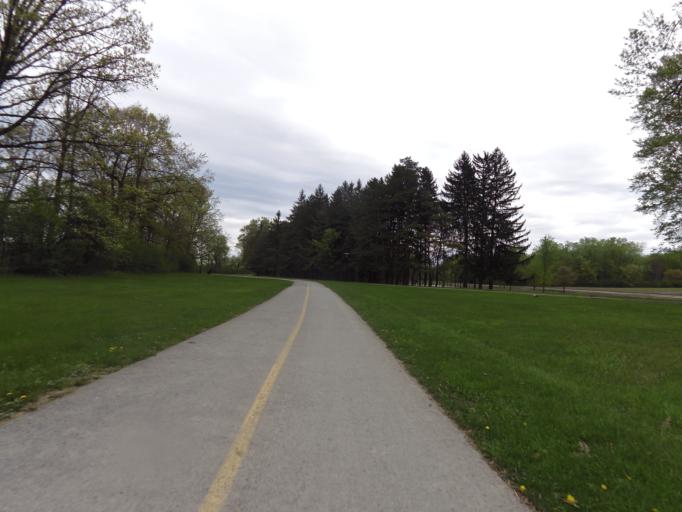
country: CA
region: Quebec
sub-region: Outaouais
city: Gatineau
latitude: 45.4551
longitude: -75.7137
